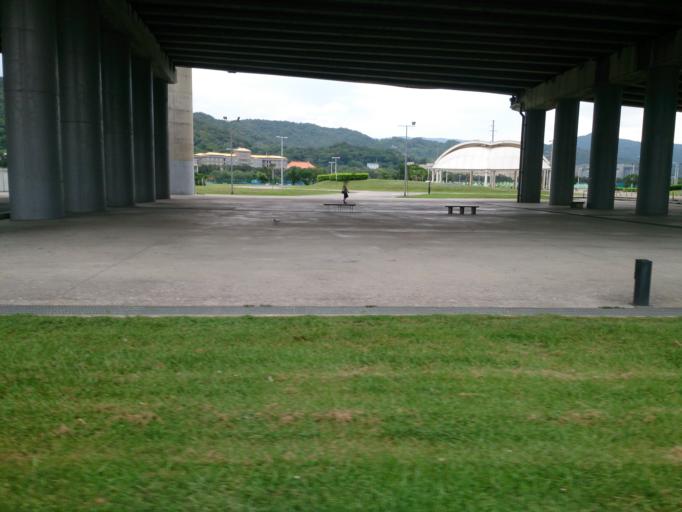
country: TW
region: Taipei
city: Taipei
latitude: 25.0735
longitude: 121.5291
